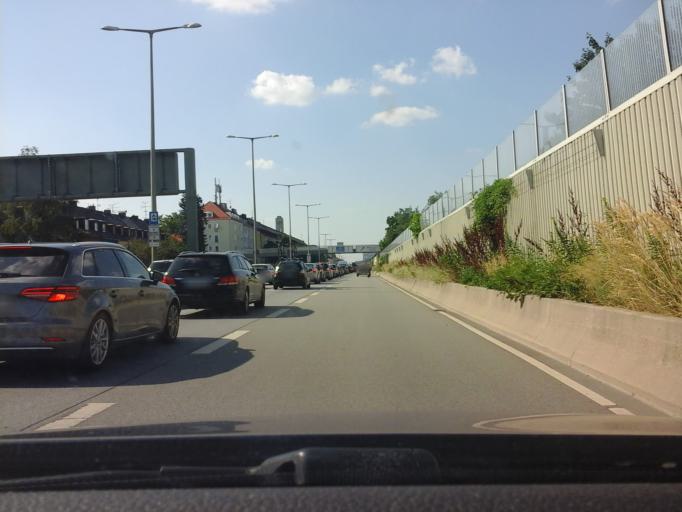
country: DE
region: Bavaria
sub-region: Upper Bavaria
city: Unterhaching
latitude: 48.0956
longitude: 11.5879
